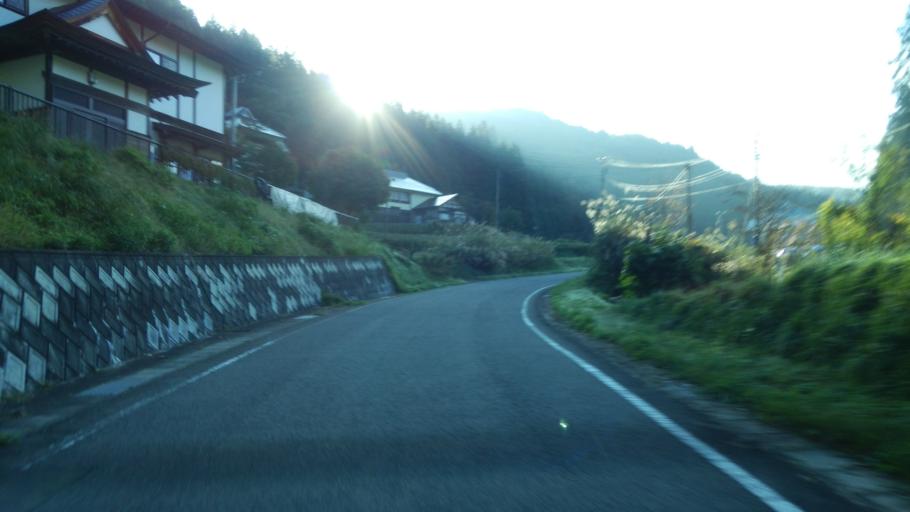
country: JP
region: Fukushima
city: Kitakata
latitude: 37.4192
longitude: 139.7284
